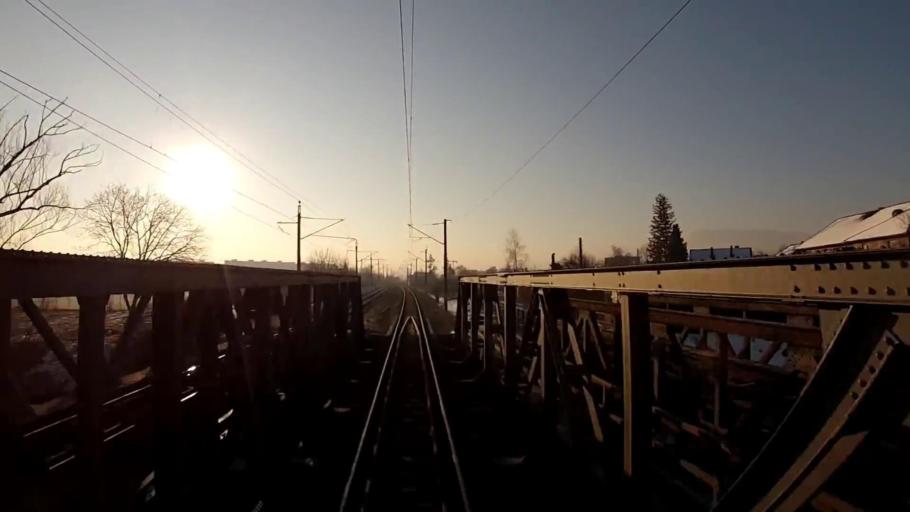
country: BG
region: Sofiya
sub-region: Obshtina Bozhurishte
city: Bozhurishte
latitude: 42.7486
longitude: 23.2522
